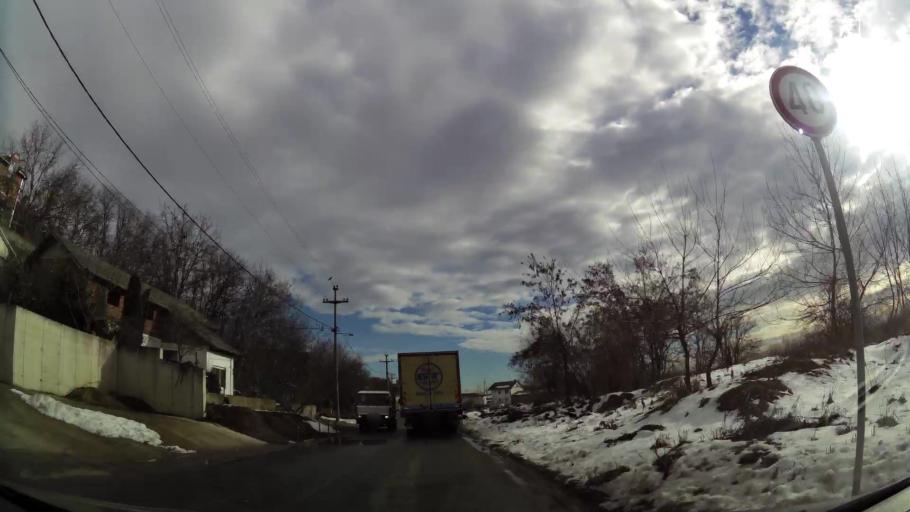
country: RS
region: Central Serbia
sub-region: Belgrade
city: Surcin
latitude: 44.7948
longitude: 20.3185
